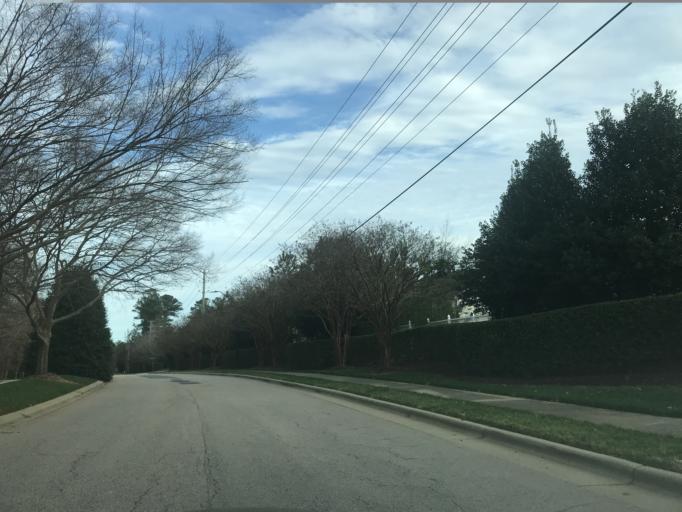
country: US
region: North Carolina
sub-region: Wake County
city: Wake Forest
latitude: 35.9254
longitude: -78.5837
